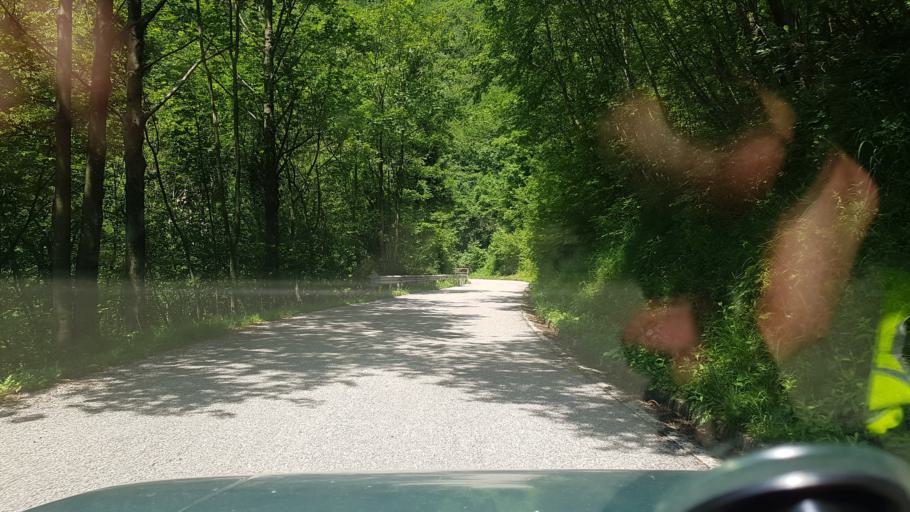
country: IT
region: Friuli Venezia Giulia
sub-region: Provincia di Udine
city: Lusevera
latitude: 46.2751
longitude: 13.3019
